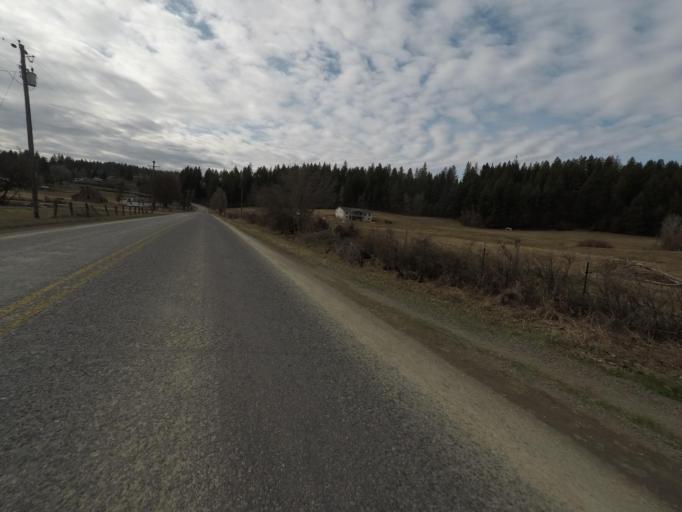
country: US
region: Washington
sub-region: Stevens County
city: Colville
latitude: 48.5152
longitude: -117.8685
